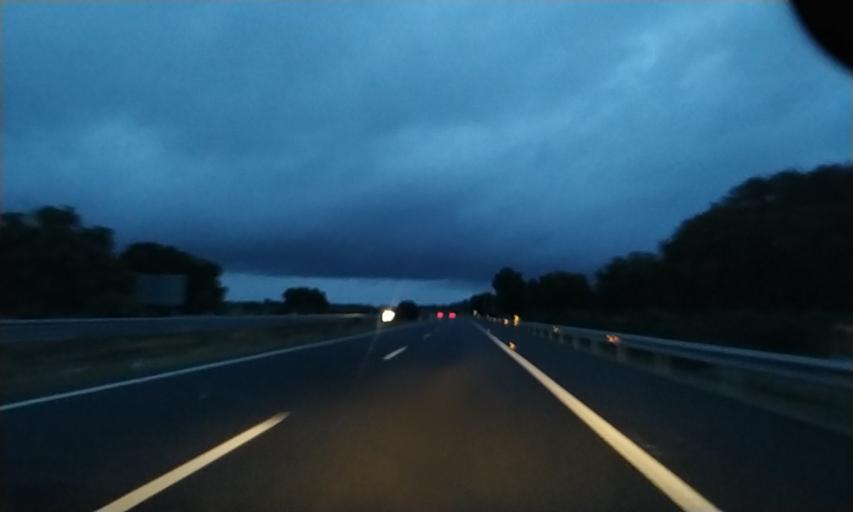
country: ES
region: Extremadura
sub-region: Provincia de Caceres
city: Aldea del Cano
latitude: 39.3011
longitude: -6.3294
